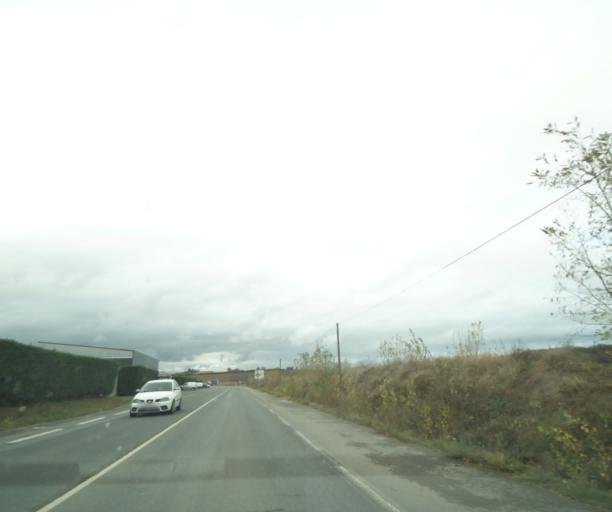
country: FR
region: Auvergne
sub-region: Departement du Puy-de-Dome
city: Pont-du-Chateau
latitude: 45.8166
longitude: 3.2613
